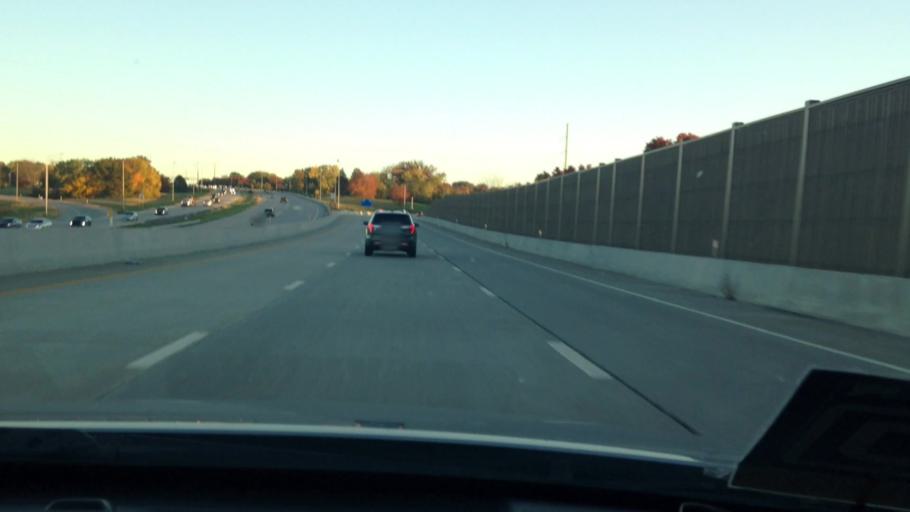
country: US
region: Kansas
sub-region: Johnson County
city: Lenexa
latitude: 38.9168
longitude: -94.7024
